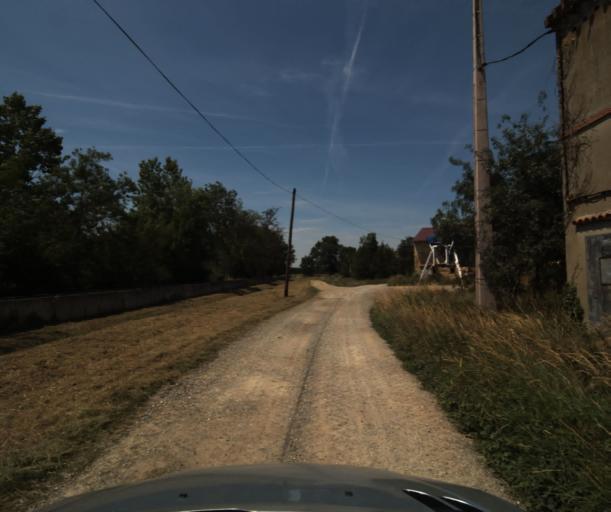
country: FR
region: Midi-Pyrenees
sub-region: Departement de la Haute-Garonne
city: Labastidette
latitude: 43.4525
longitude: 1.2349
